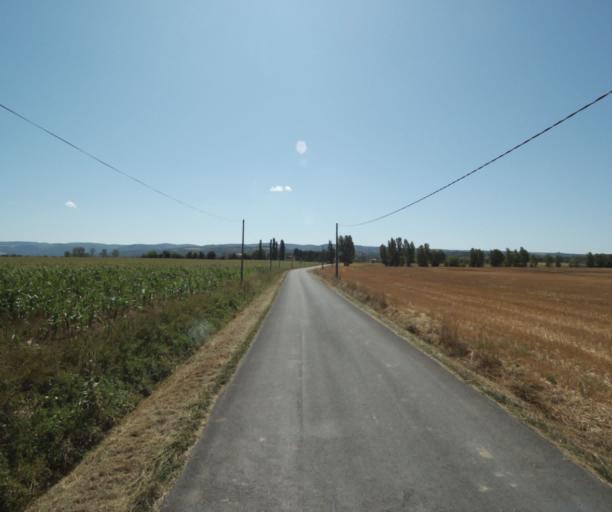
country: FR
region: Midi-Pyrenees
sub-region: Departement de la Haute-Garonne
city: Revel
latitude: 43.4624
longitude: 1.9690
